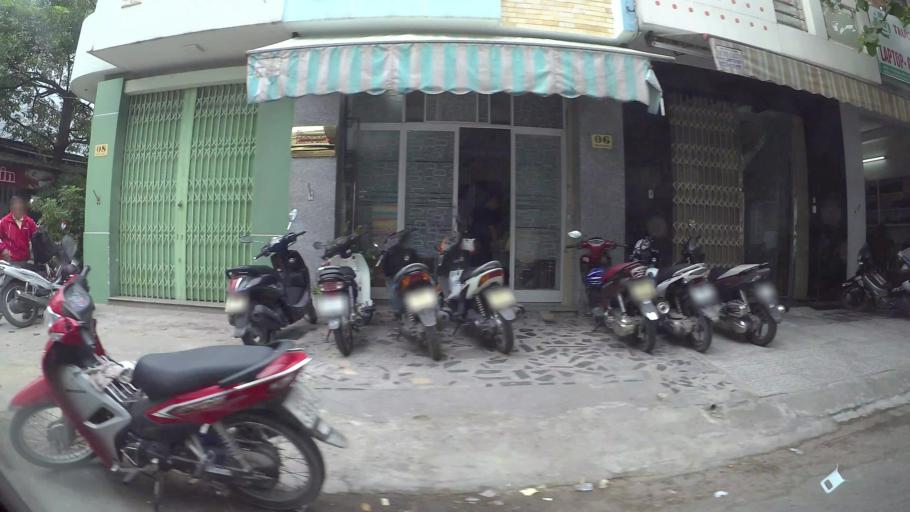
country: VN
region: Da Nang
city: Thanh Khe
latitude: 16.0713
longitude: 108.1946
